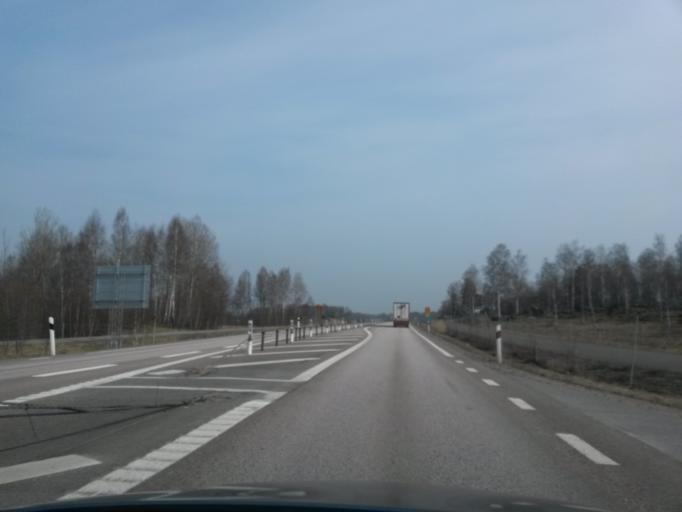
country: SE
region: Vaestra Goetaland
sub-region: Mariestads Kommun
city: Mariestad
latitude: 58.7517
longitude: 13.9576
